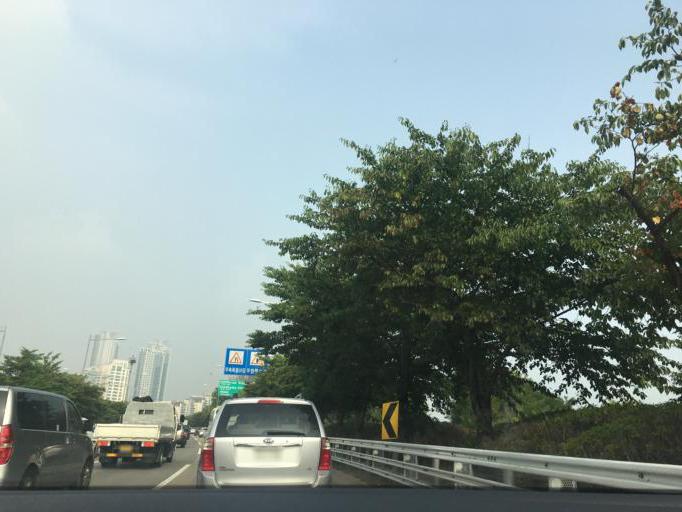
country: KR
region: Gyeonggi-do
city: Seongnam-si
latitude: 37.5183
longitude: 127.0731
